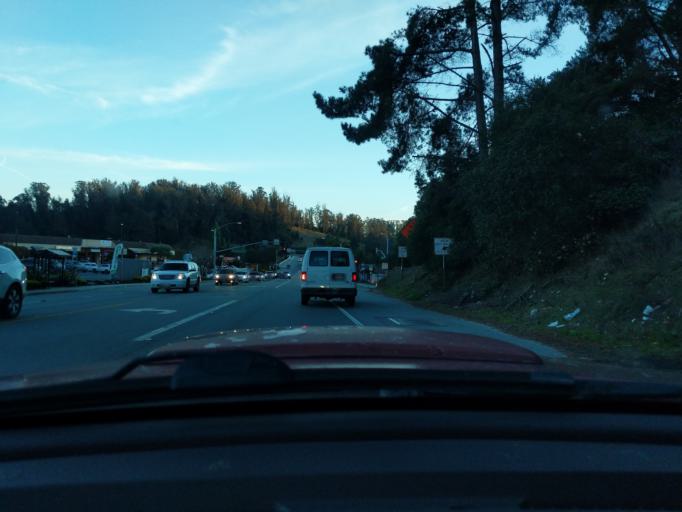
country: US
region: California
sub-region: Monterey County
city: Prunedale
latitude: 36.8024
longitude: -121.6665
